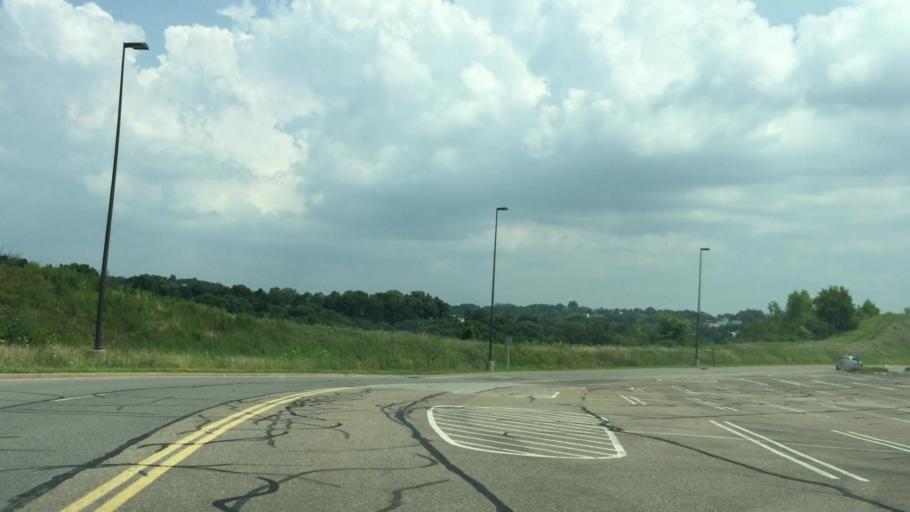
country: US
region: Pennsylvania
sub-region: Allegheny County
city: Rennerdale
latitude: 40.4577
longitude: -80.1569
